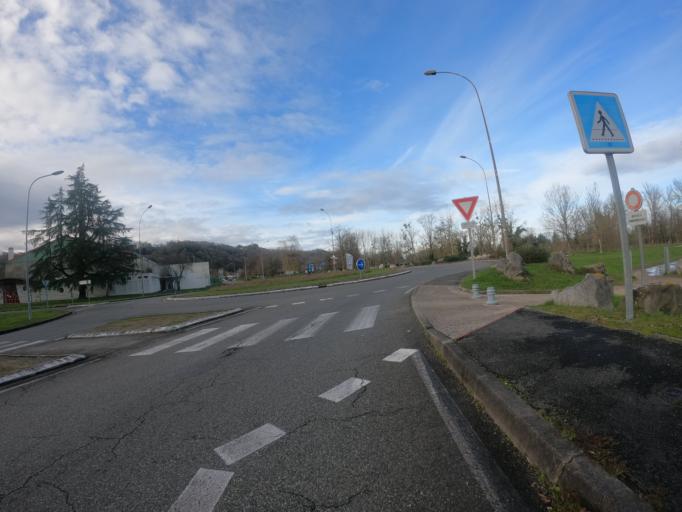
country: FR
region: Aquitaine
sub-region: Departement des Pyrenees-Atlantiques
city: Billere
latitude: 43.2927
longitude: -0.3963
